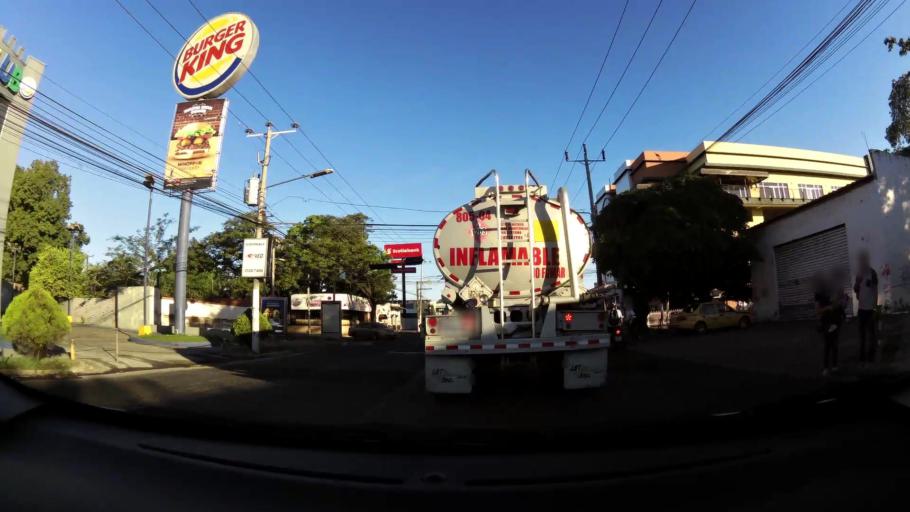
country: SV
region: San Miguel
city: San Miguel
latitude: 13.4757
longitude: -88.1842
